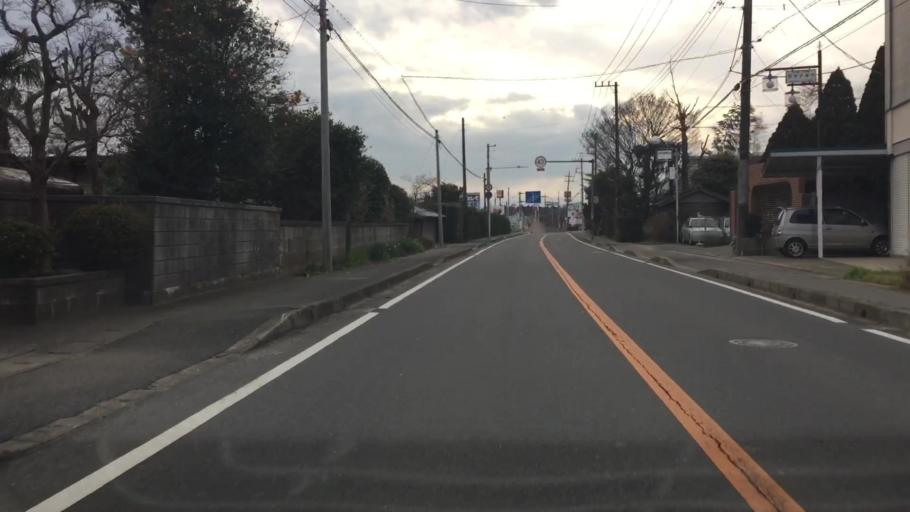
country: JP
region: Chiba
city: Shiroi
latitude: 35.7863
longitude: 140.0493
